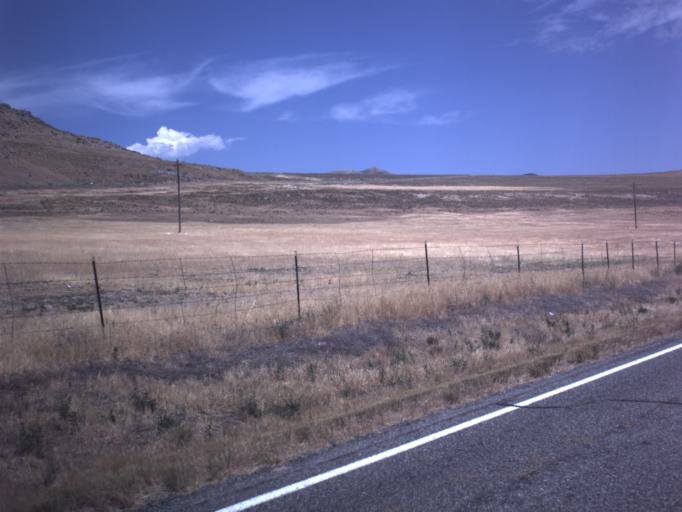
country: US
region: Utah
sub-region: Box Elder County
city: Tremonton
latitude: 41.6184
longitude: -112.3650
